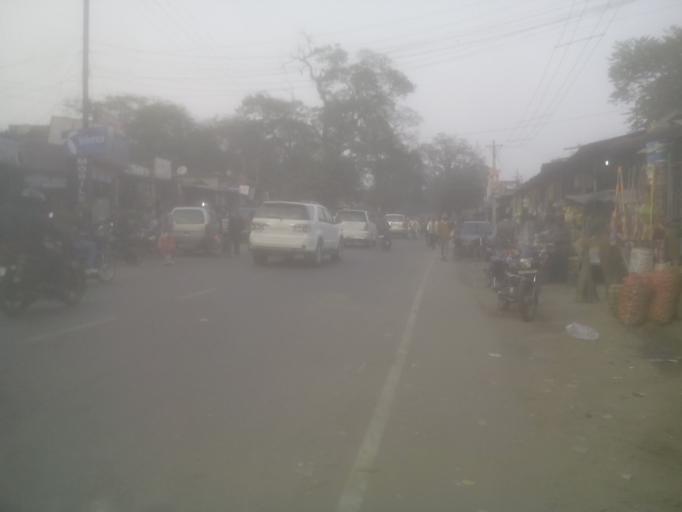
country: IN
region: Jharkhand
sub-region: Dhanbad
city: Dhanbad
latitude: 23.8076
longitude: 86.4320
